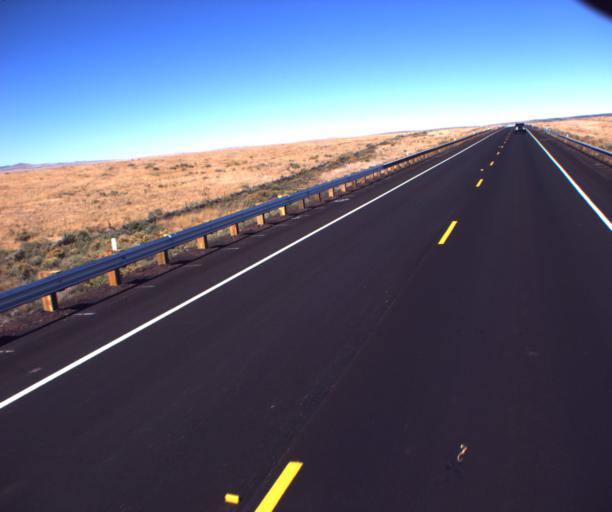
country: US
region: Arizona
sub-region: Apache County
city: Springerville
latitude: 34.2568
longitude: -109.3543
